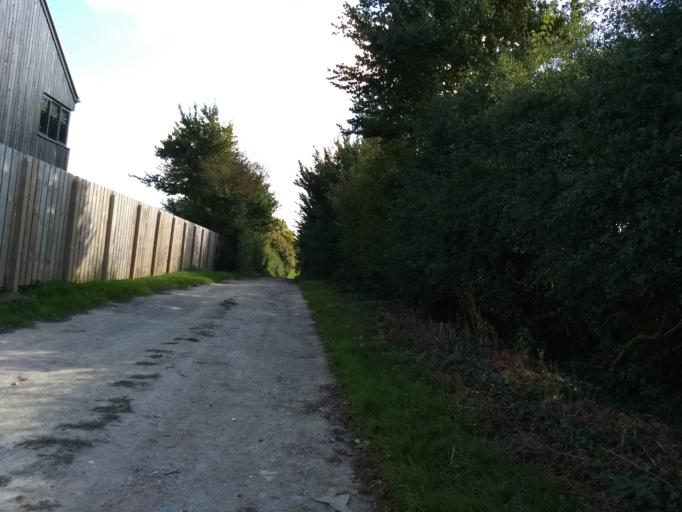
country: GB
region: England
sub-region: Isle of Wight
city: Seaview
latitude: 50.7079
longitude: -1.1268
